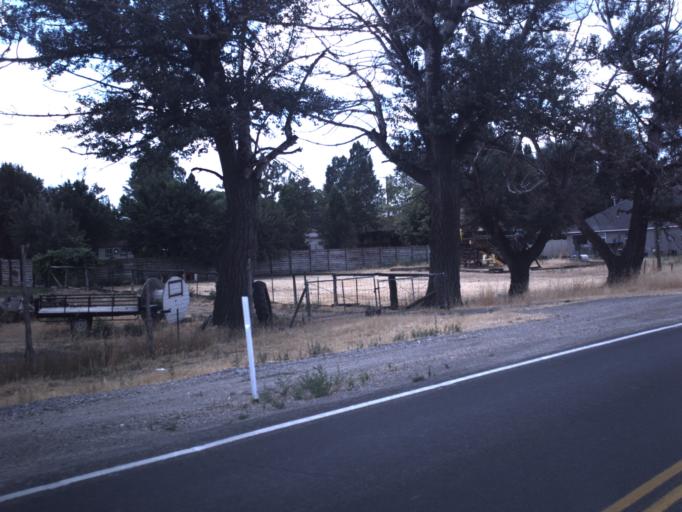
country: US
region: Utah
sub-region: Juab County
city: Mona
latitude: 39.8192
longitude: -111.8502
